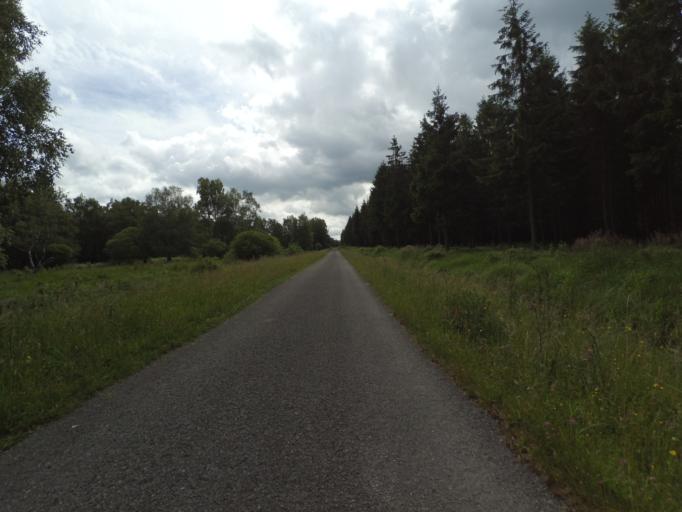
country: DE
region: North Rhine-Westphalia
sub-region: Regierungsbezirk Koln
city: Roetgen
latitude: 50.5888
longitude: 6.1733
